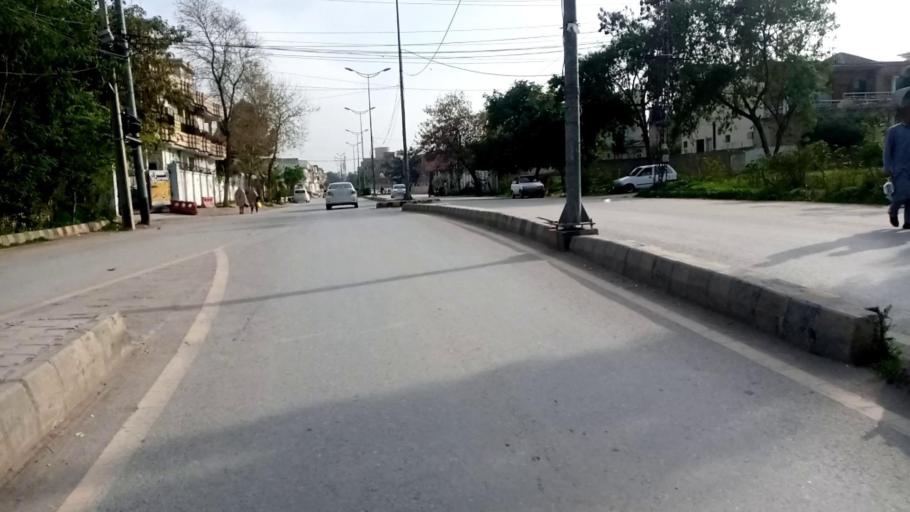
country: PK
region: Khyber Pakhtunkhwa
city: Peshawar
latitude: 33.9958
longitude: 71.4526
